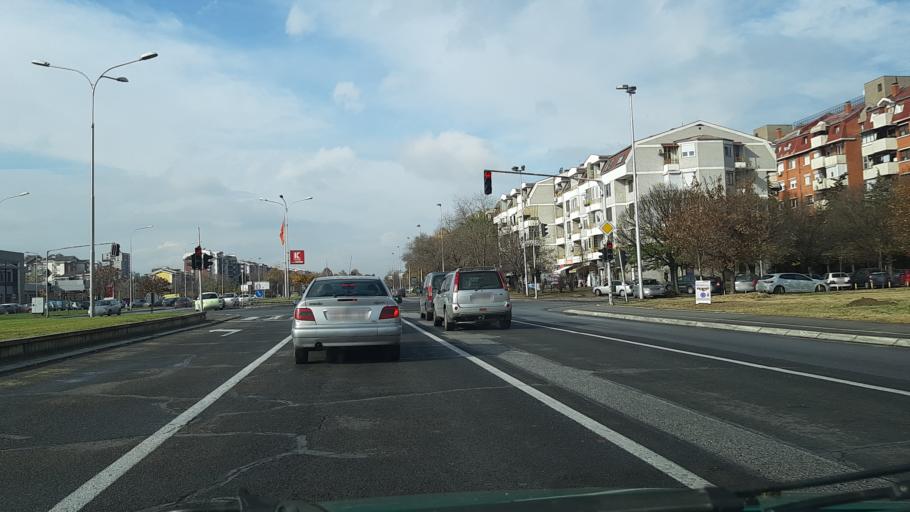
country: MK
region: Kisela Voda
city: Usje
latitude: 41.9814
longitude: 21.4742
